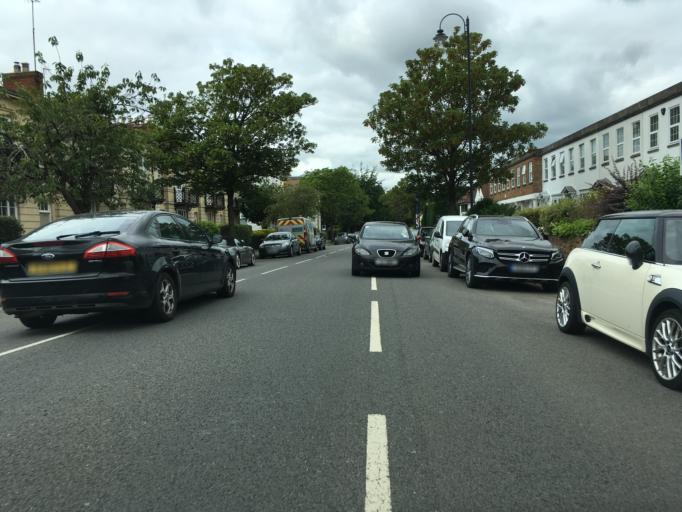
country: GB
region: England
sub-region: Gloucestershire
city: Cheltenham
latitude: 51.8926
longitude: -2.0878
